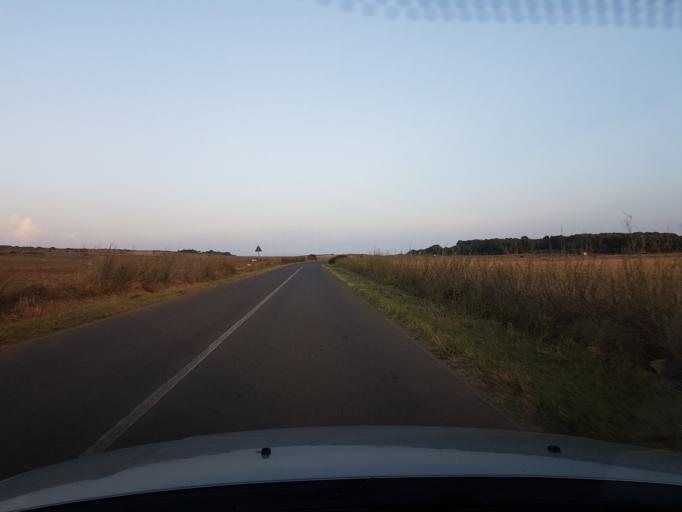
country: IT
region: Sardinia
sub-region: Provincia di Oristano
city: Cabras
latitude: 39.9408
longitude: 8.4391
